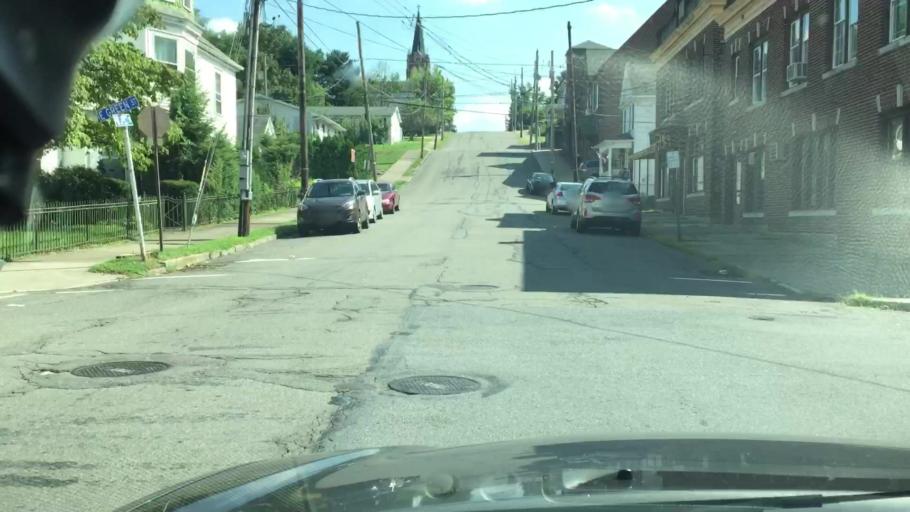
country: US
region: Pennsylvania
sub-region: Luzerne County
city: Nanticoke
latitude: 41.2021
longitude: -76.0019
